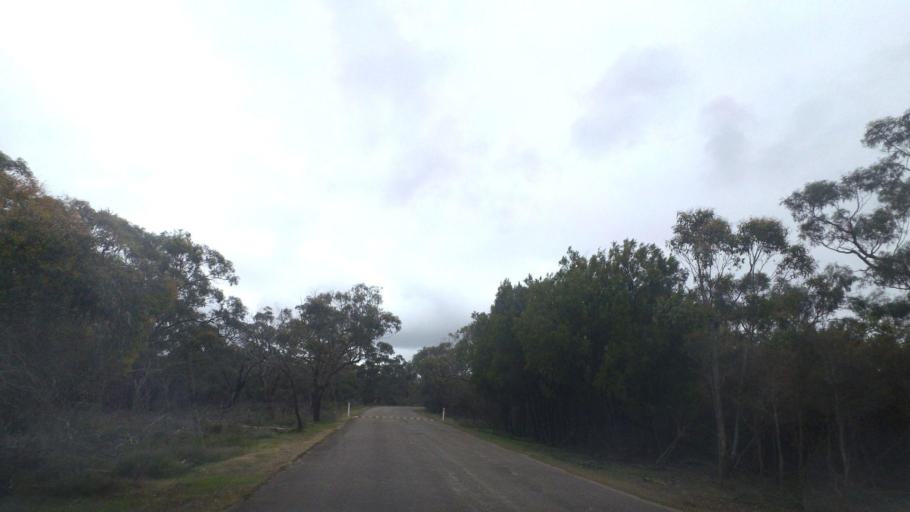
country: AU
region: Victoria
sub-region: Casey
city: Junction Village
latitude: -38.1339
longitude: 145.2827
